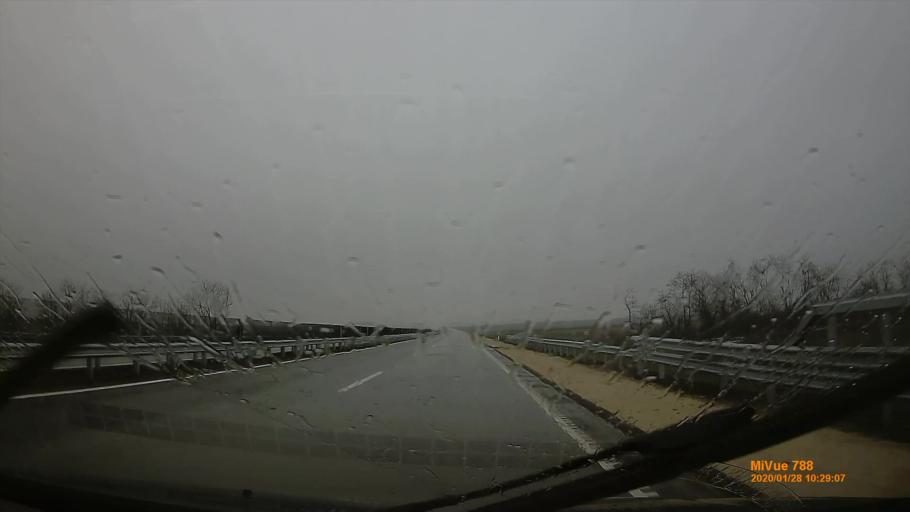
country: HU
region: Pest
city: Pilis
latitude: 47.3221
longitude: 19.5380
